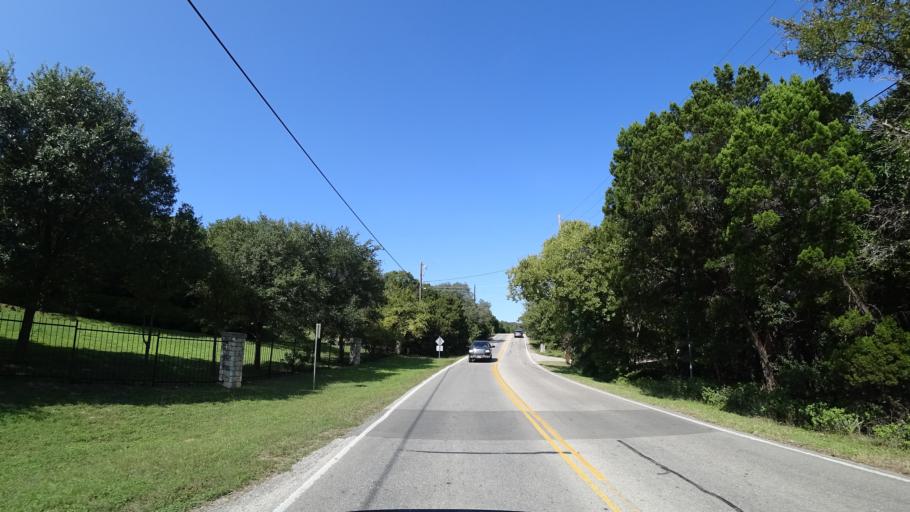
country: US
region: Texas
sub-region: Travis County
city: West Lake Hills
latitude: 30.2862
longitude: -97.8061
